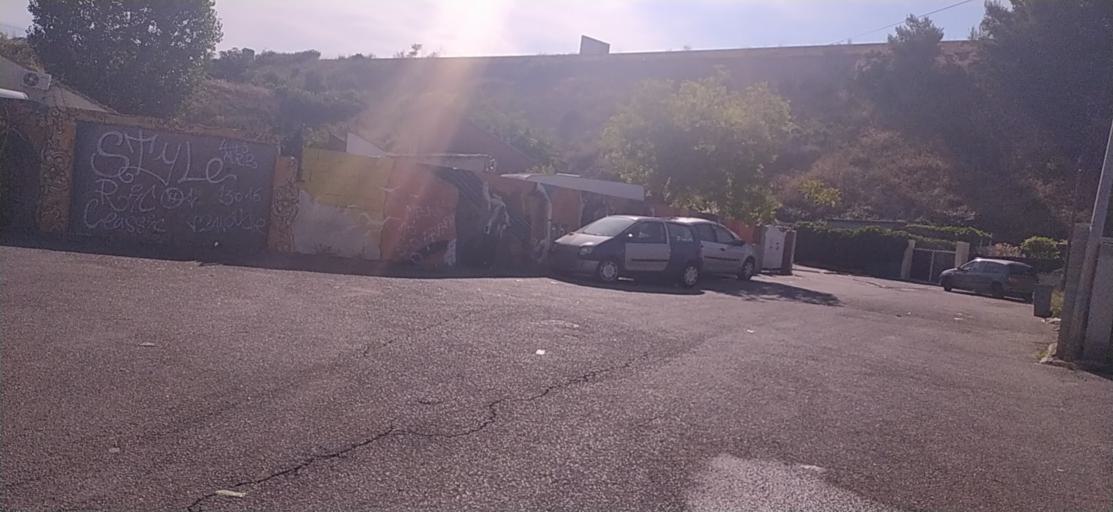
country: FR
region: Provence-Alpes-Cote d'Azur
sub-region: Departement des Bouches-du-Rhone
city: Marseille 16
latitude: 43.3499
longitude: 5.3448
